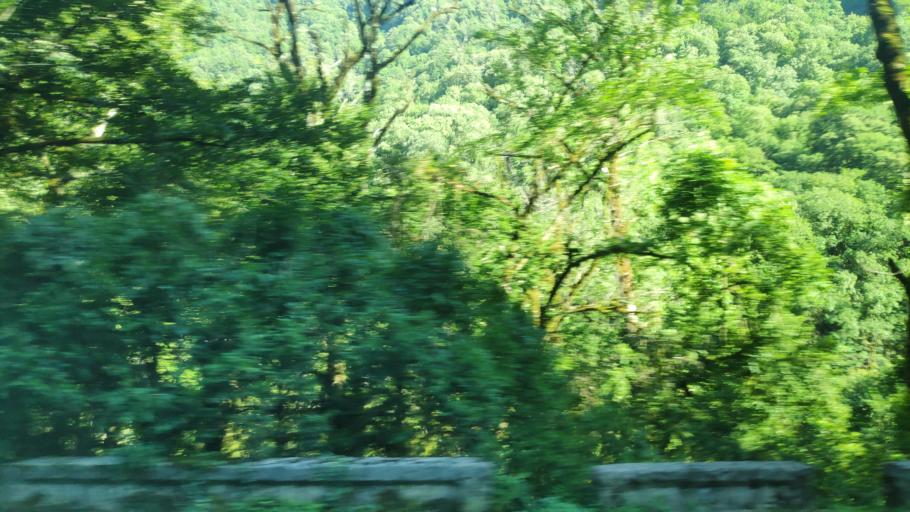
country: GE
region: Abkhazia
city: Gagra
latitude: 43.3532
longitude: 40.4195
